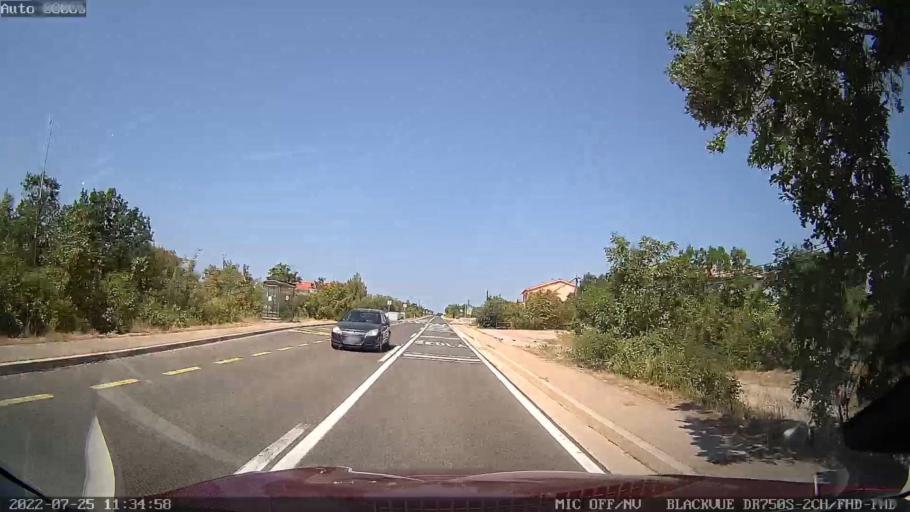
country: HR
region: Zadarska
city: Posedarje
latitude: 44.2317
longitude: 15.4152
